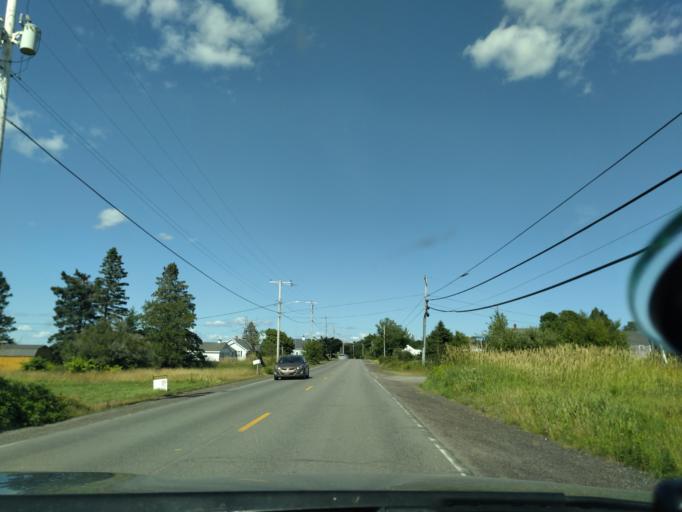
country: US
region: Maine
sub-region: Washington County
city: Eastport
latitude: 44.8505
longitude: -66.9984
